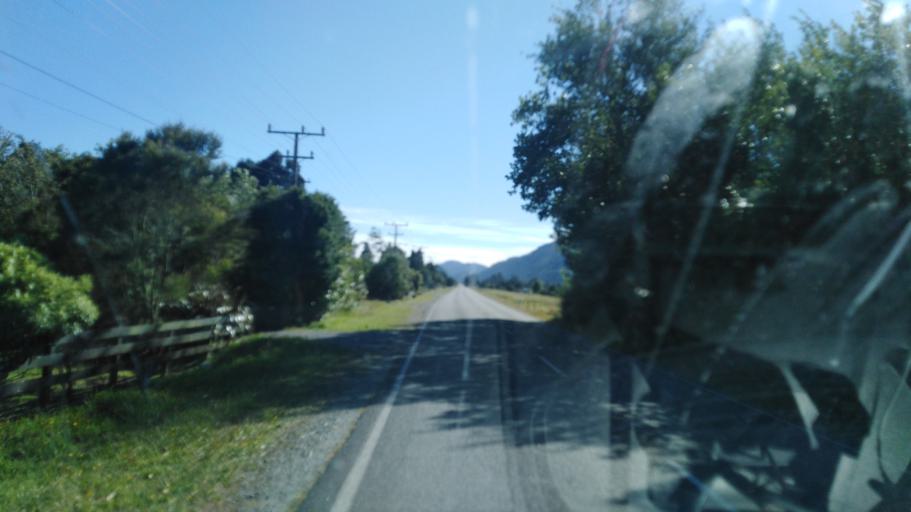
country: NZ
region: West Coast
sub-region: Buller District
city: Westport
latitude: -41.6764
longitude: 171.7979
